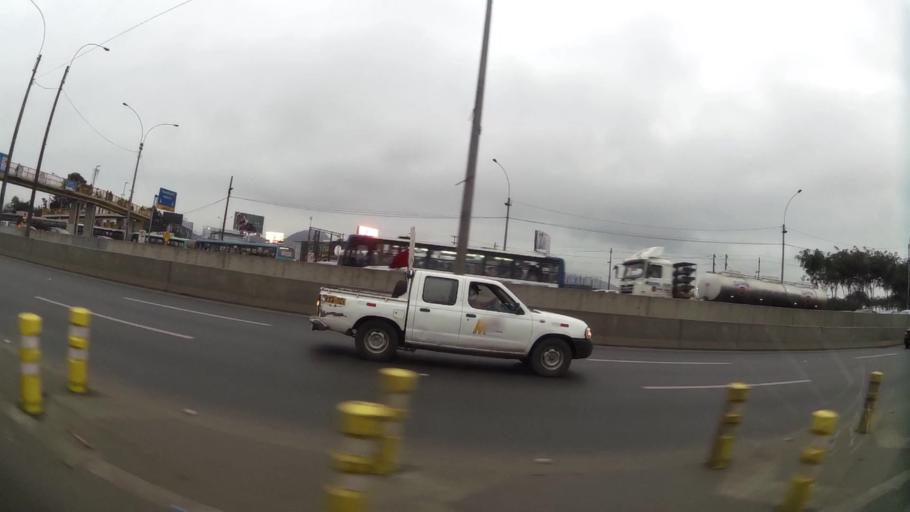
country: PE
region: Lima
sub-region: Lima
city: San Luis
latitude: -12.0840
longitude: -76.9814
